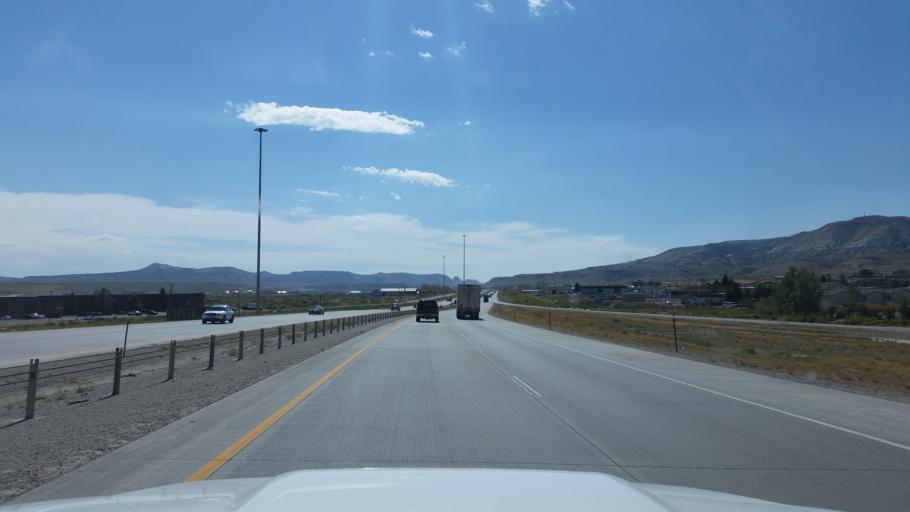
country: US
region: Wyoming
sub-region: Sweetwater County
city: Rock Springs
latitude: 41.5787
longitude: -109.2576
